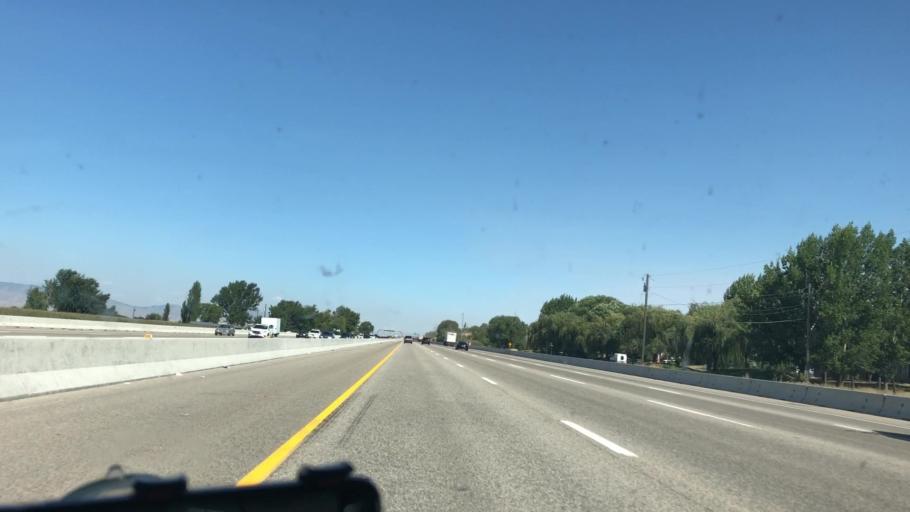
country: US
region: Idaho
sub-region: Ada County
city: Meridian
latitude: 43.5976
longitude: -116.4787
